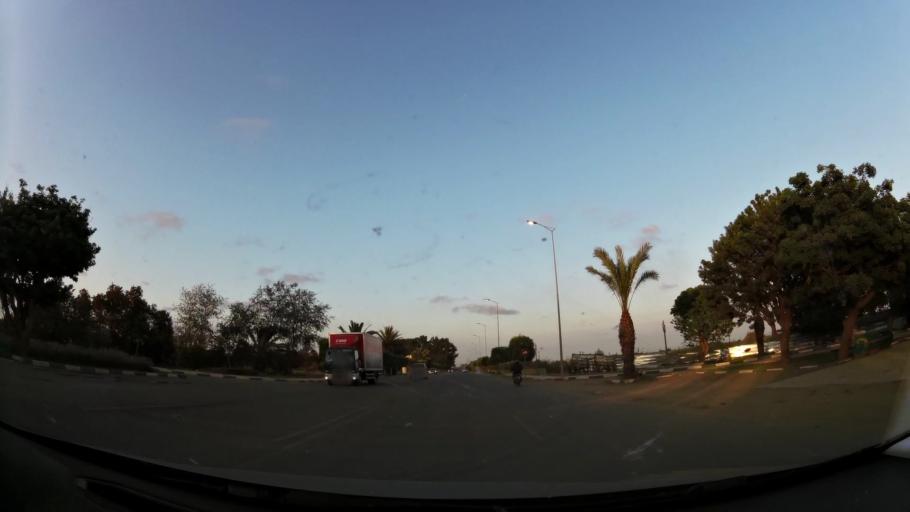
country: MA
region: Gharb-Chrarda-Beni Hssen
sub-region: Kenitra Province
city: Kenitra
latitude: 34.2765
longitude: -6.5535
